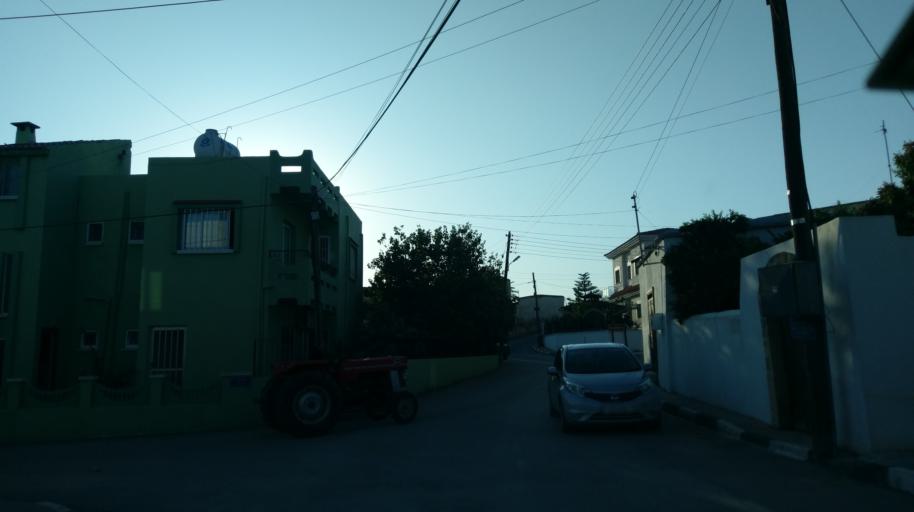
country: CY
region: Ammochostos
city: Trikomo
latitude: 35.3657
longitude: 33.9383
